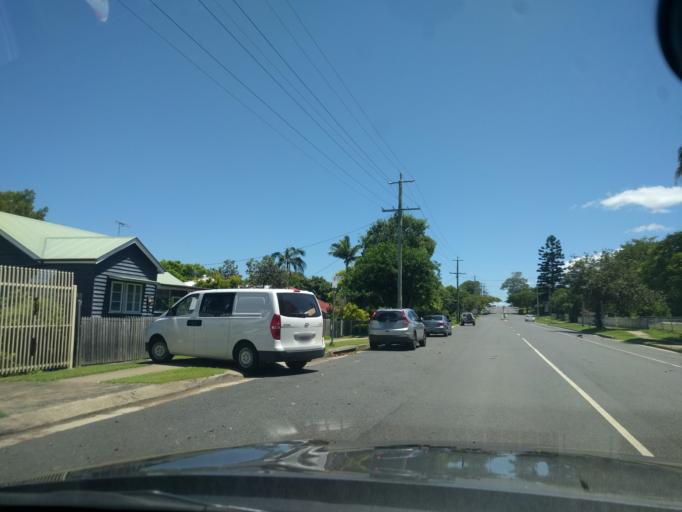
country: AU
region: Queensland
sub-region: Logan
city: Cedar Vale
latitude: -27.9888
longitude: 153.0023
